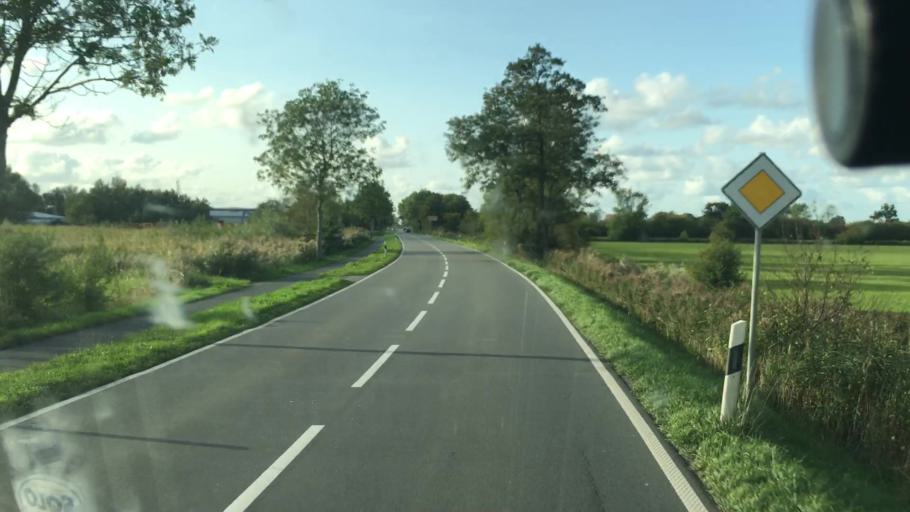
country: DE
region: Lower Saxony
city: Jever
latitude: 53.5887
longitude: 7.8751
